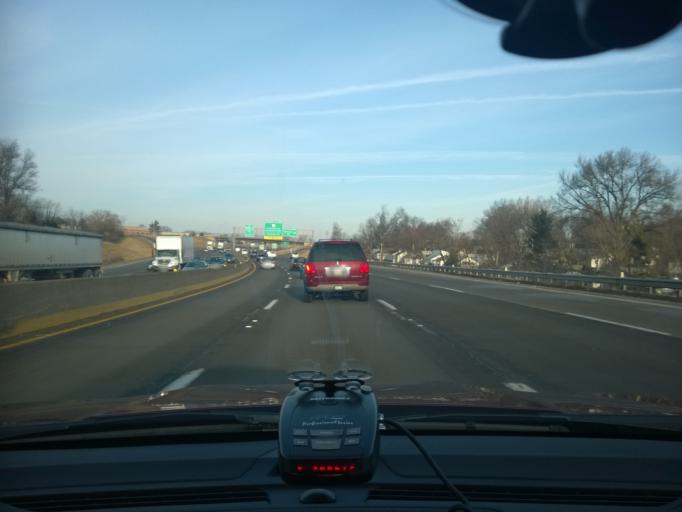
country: US
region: Missouri
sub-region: Saint Louis County
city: Normandy
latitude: 38.7156
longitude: -90.2932
